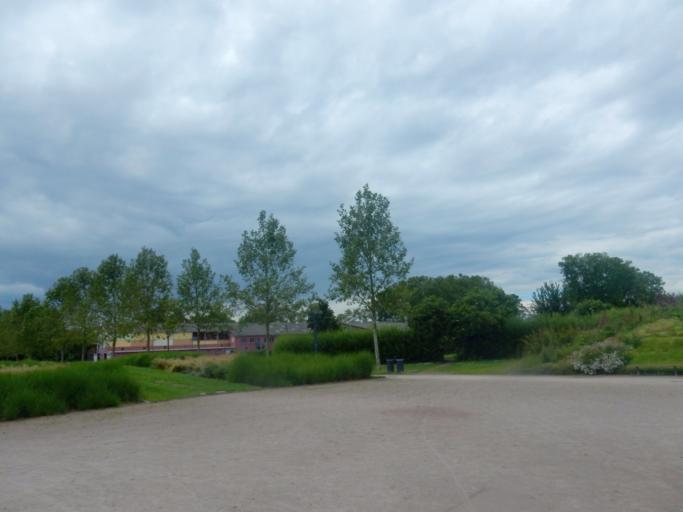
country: DE
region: Baden-Wuerttemberg
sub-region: Freiburg Region
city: Kehl
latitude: 48.5683
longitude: 7.7985
